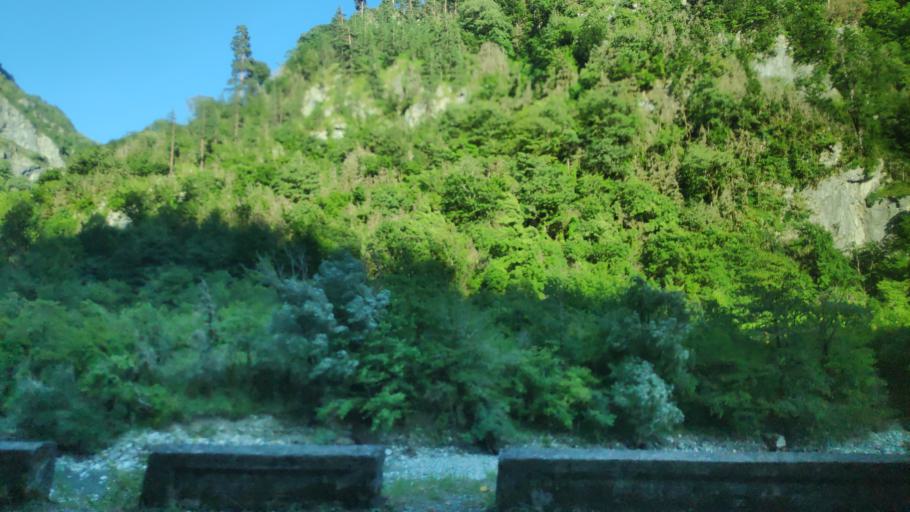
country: GE
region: Abkhazia
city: Gagra
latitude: 43.3674
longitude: 40.4567
